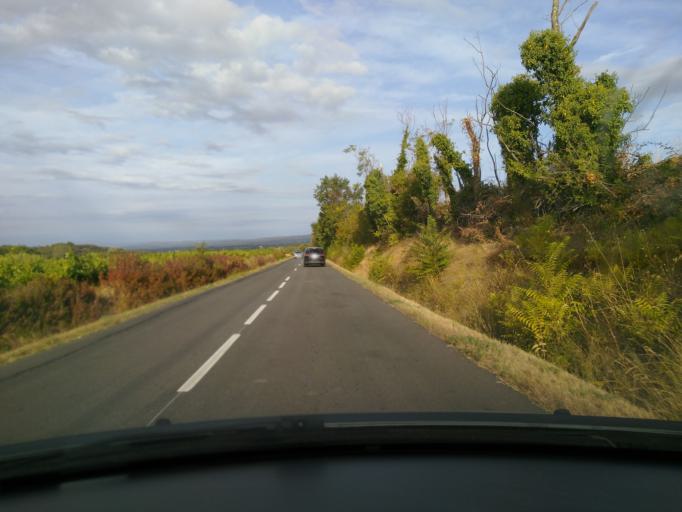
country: FR
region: Rhone-Alpes
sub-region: Departement de la Drome
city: Taulignan
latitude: 44.4270
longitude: 5.0350
